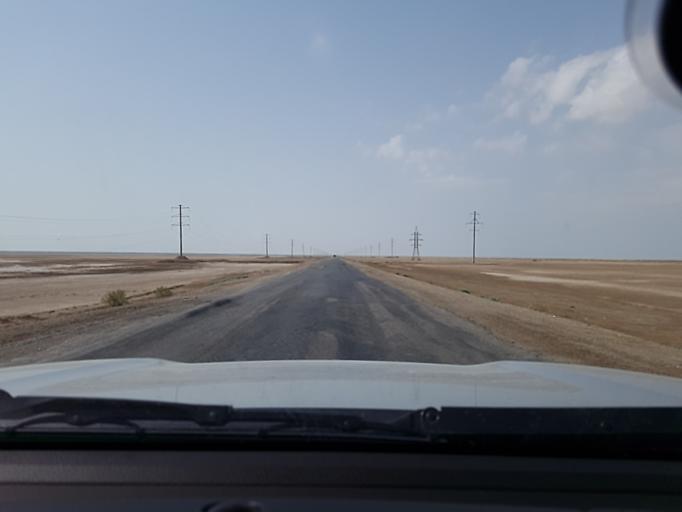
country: TM
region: Balkan
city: Gumdag
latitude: 39.0847
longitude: 54.5844
